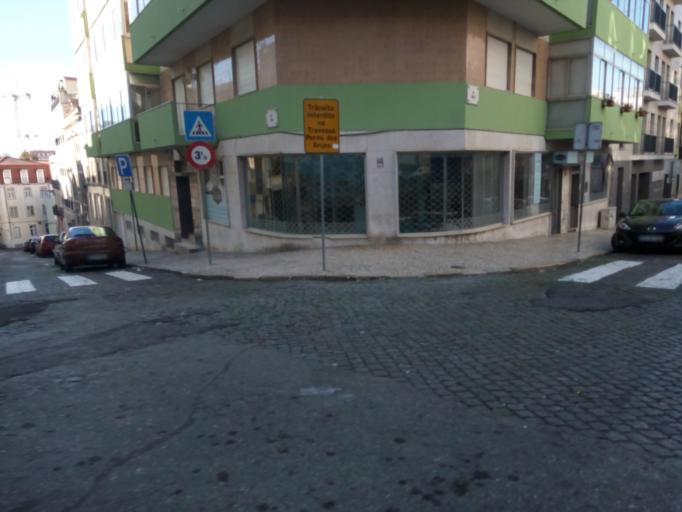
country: PT
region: Lisbon
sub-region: Lisbon
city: Lisbon
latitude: 38.7225
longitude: -9.1334
